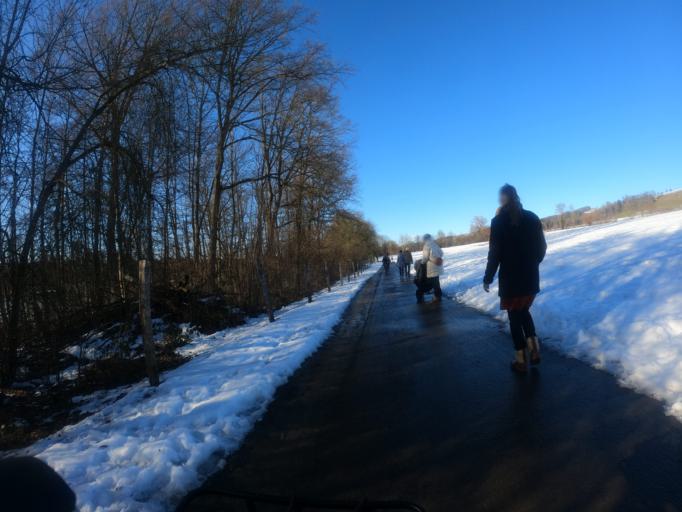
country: CH
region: Aargau
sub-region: Bezirk Bremgarten
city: Unterlunkhofen
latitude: 47.3252
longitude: 8.3744
